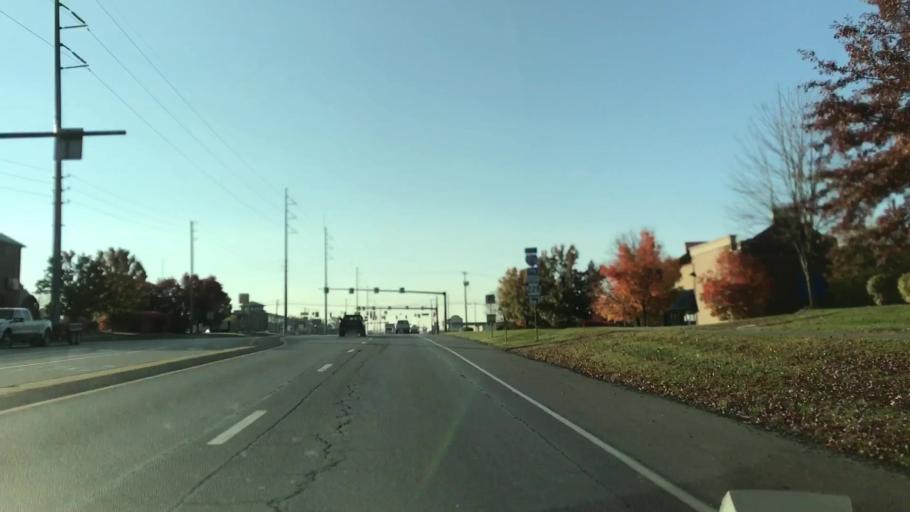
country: US
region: Pennsylvania
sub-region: Butler County
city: Cranberry Township
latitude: 40.6871
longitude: -80.1020
